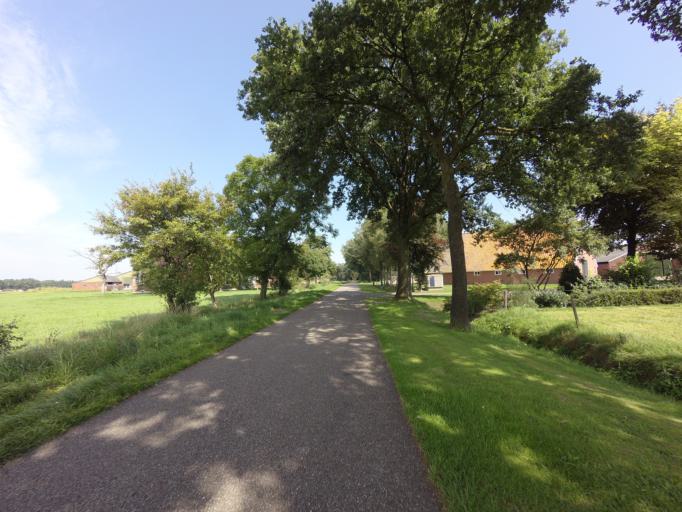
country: NL
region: Overijssel
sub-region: Gemeente Hof van Twente
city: Hengevelde
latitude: 52.1766
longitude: 6.6262
